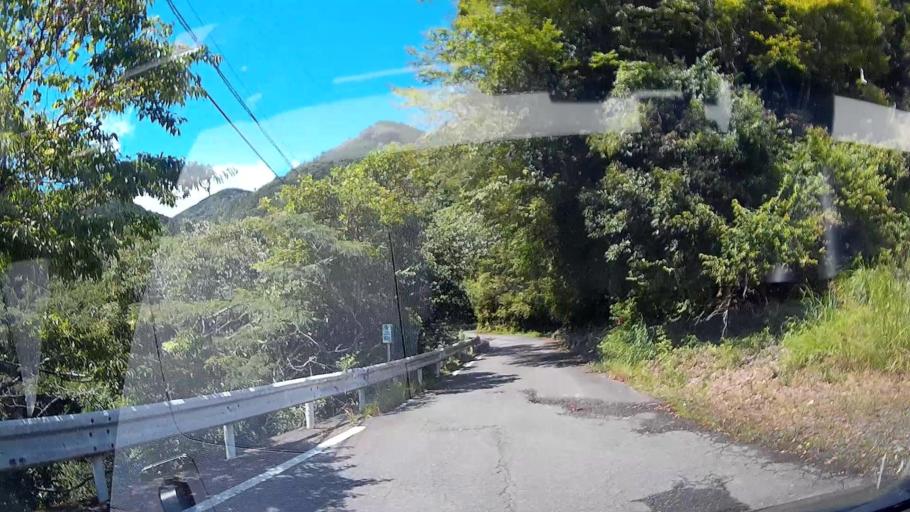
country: JP
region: Shizuoka
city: Shizuoka-shi
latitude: 35.1763
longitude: 138.2954
